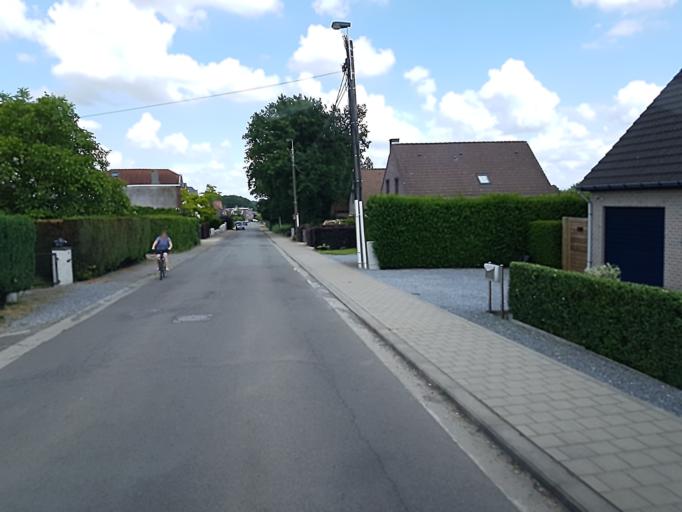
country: BE
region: Flanders
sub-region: Provincie Vlaams-Brabant
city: Hoeilaart
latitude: 50.7617
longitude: 4.4638
